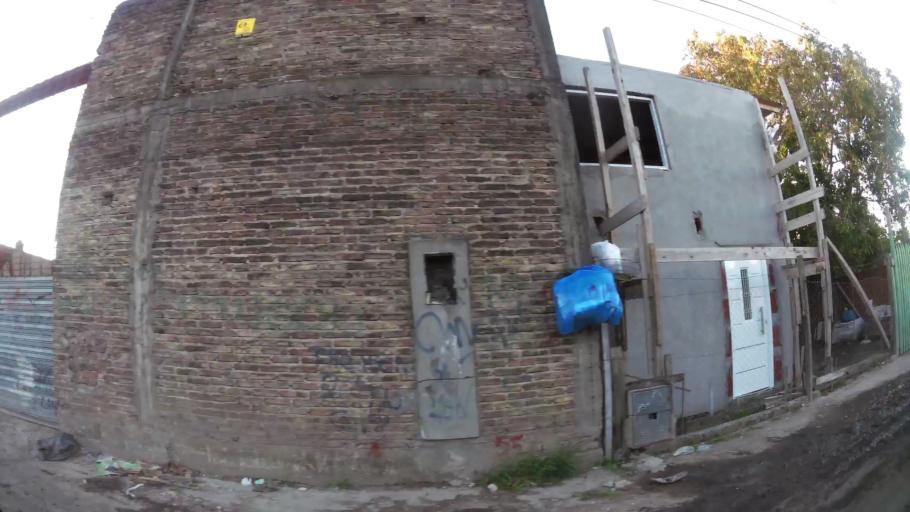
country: AR
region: Buenos Aires
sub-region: Partido de Almirante Brown
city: Adrogue
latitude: -34.7811
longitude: -58.3365
